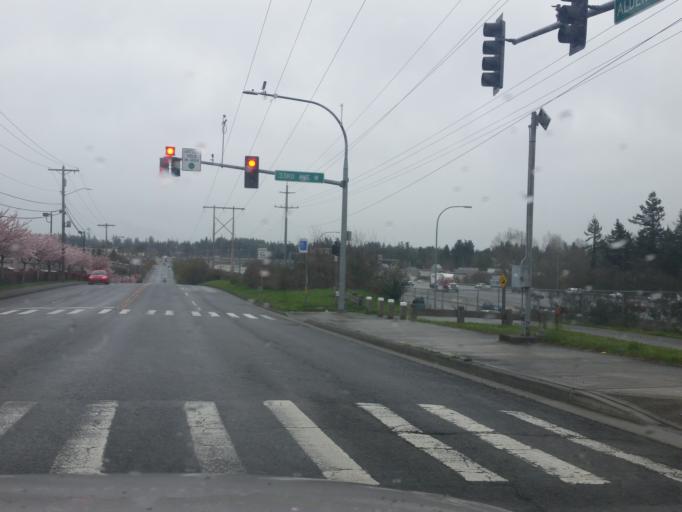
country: US
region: Washington
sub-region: Snohomish County
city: Alderwood Manor
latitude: 47.8226
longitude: -122.2777
